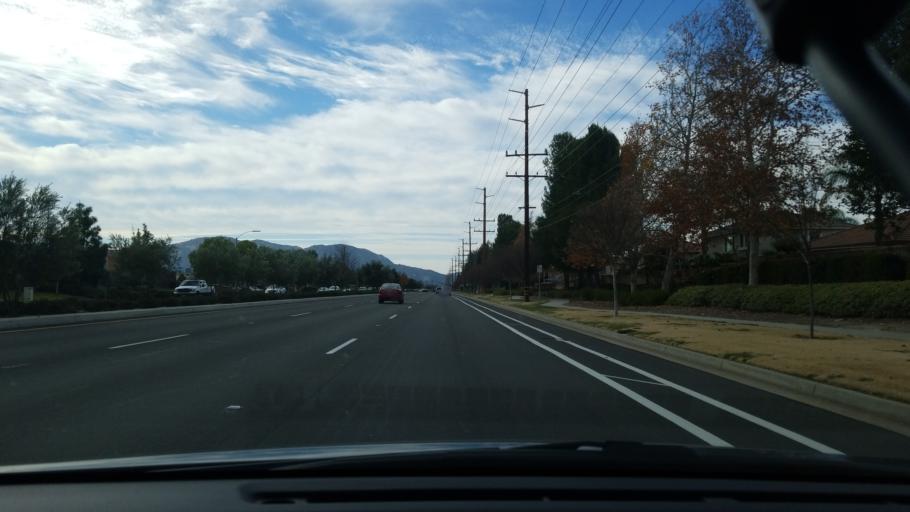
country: US
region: California
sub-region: Riverside County
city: Temecula
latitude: 33.4837
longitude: -117.0887
